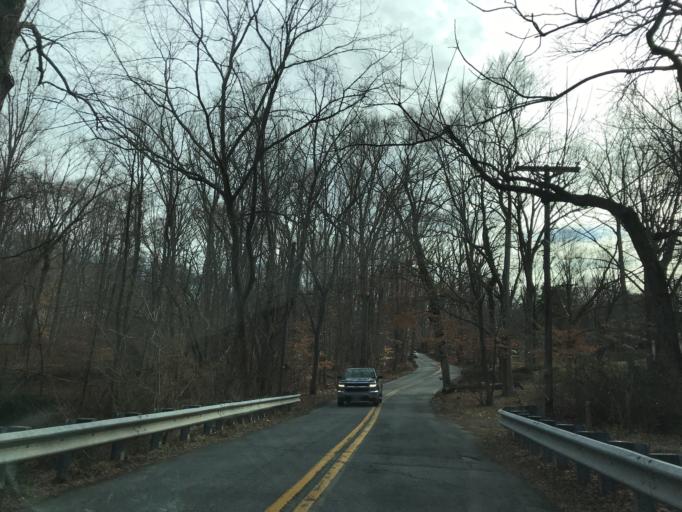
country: US
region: Maryland
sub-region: Baltimore County
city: Kingsville
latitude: 39.4438
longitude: -76.4019
